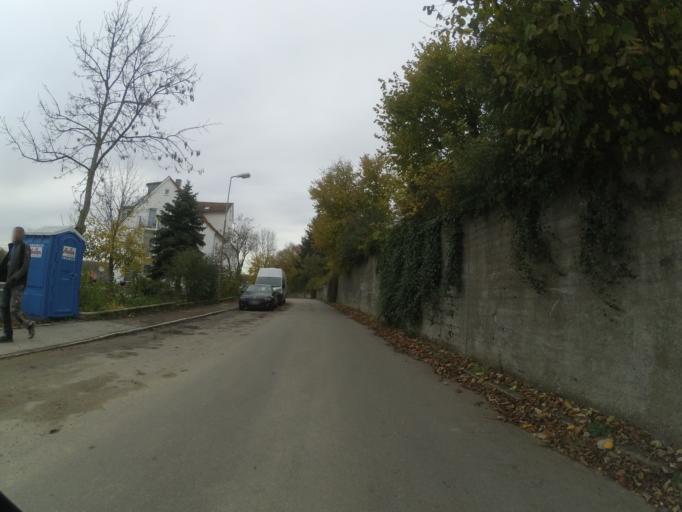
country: DE
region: Baden-Wuerttemberg
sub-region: Tuebingen Region
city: Staig
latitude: 48.3383
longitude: 10.0058
